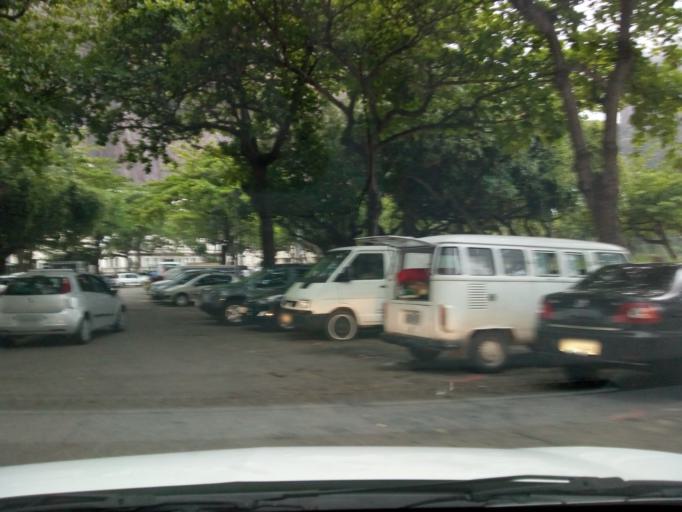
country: BR
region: Rio de Janeiro
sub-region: Rio De Janeiro
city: Rio de Janeiro
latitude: -22.9555
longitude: -43.1656
